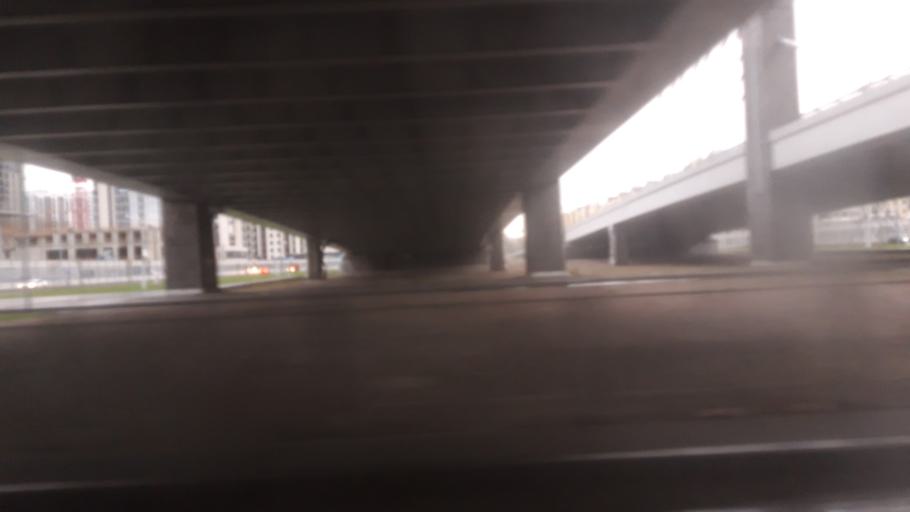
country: RU
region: St.-Petersburg
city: Kupchino
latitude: 59.8305
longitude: 30.3229
